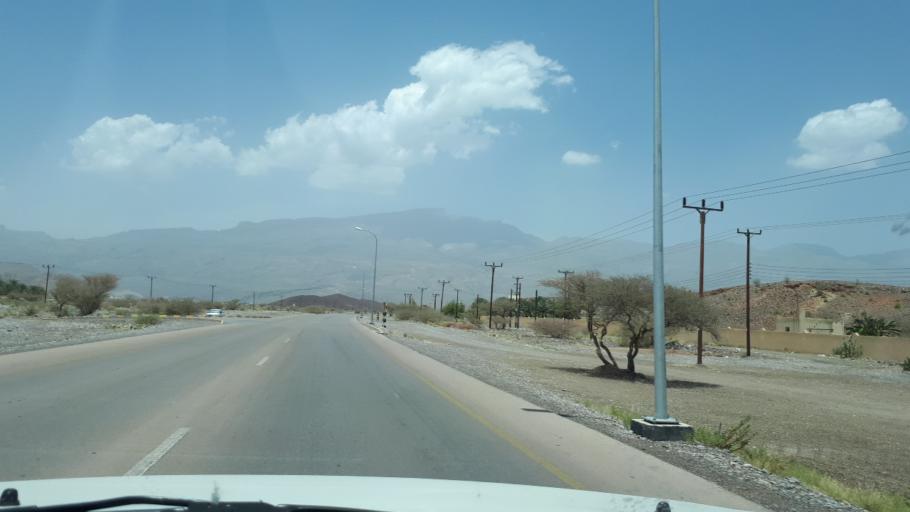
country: OM
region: Muhafazat ad Dakhiliyah
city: Bahla'
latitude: 23.0781
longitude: 57.2717
